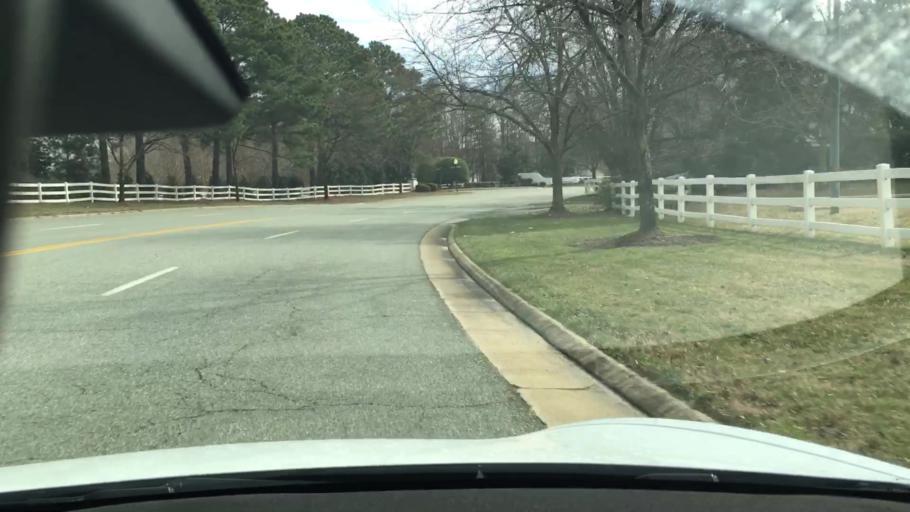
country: US
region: Virginia
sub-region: Chesterfield County
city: Bon Air
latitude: 37.5269
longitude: -77.6086
